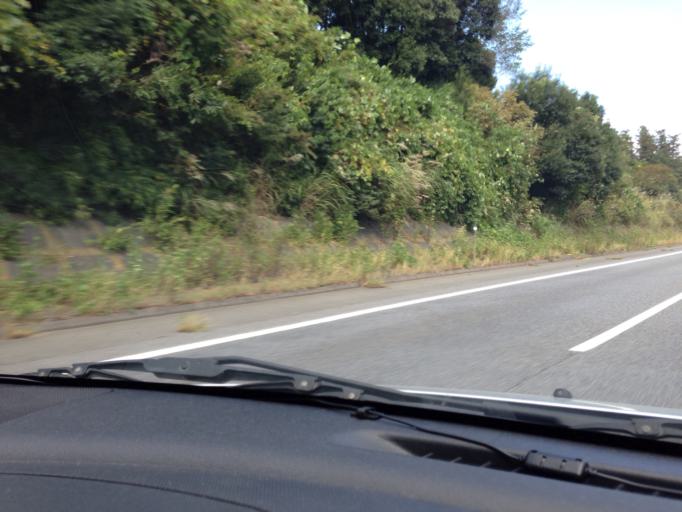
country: JP
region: Ibaraki
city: Ishioka
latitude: 36.1543
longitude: 140.2221
